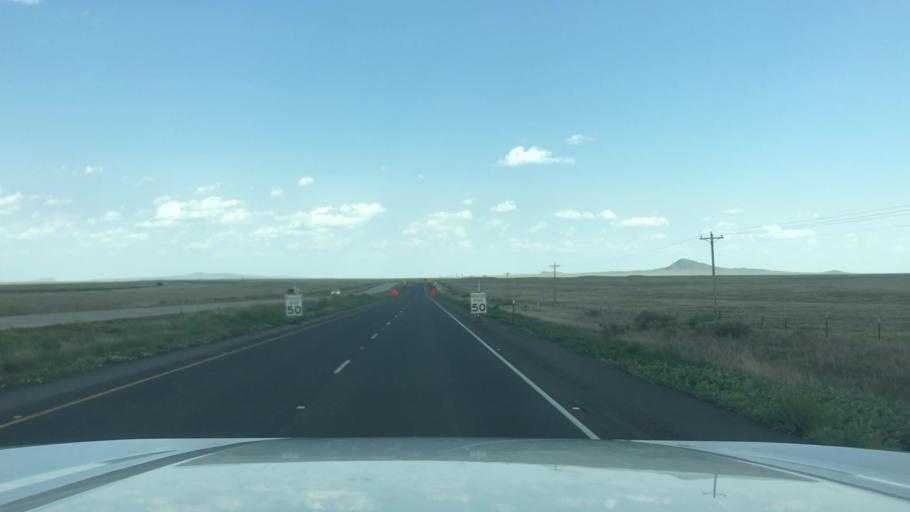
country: US
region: New Mexico
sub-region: Union County
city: Clayton
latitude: 36.6210
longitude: -103.6964
